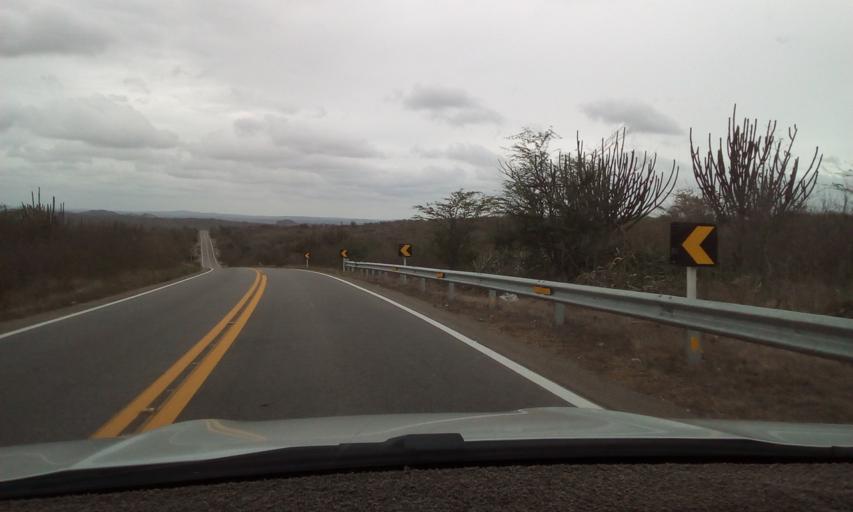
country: BR
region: Paraiba
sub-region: Areia
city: Remigio
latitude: -6.9001
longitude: -35.8822
